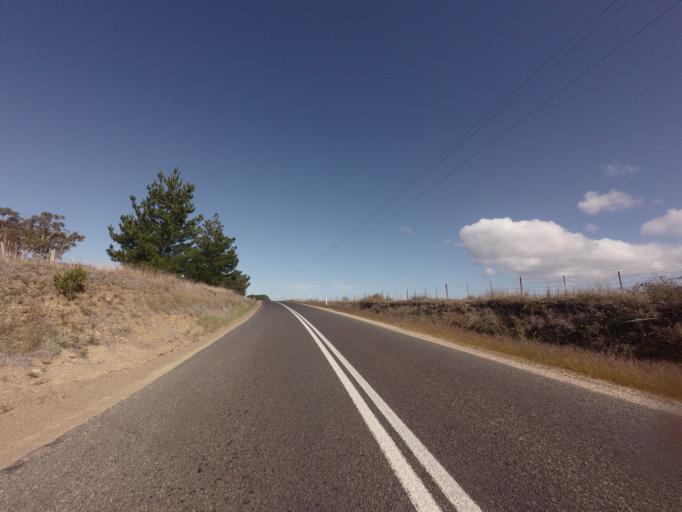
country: AU
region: Tasmania
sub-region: Break O'Day
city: St Helens
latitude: -41.7438
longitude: 148.2733
